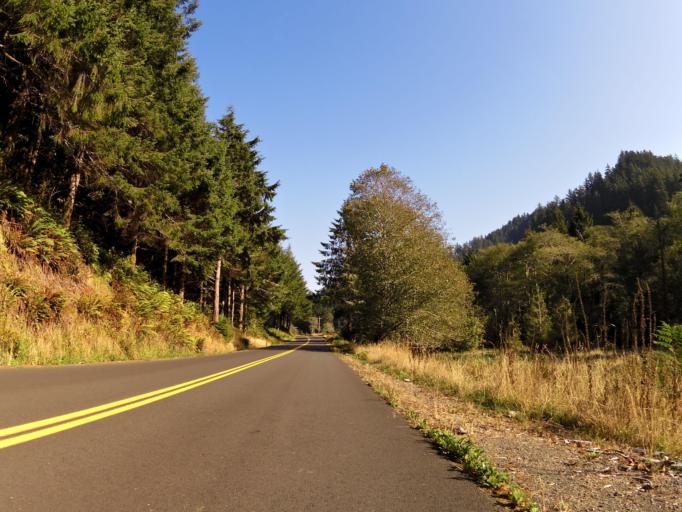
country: US
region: Oregon
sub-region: Lincoln County
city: Rose Lodge
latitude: 45.0866
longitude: -123.9619
